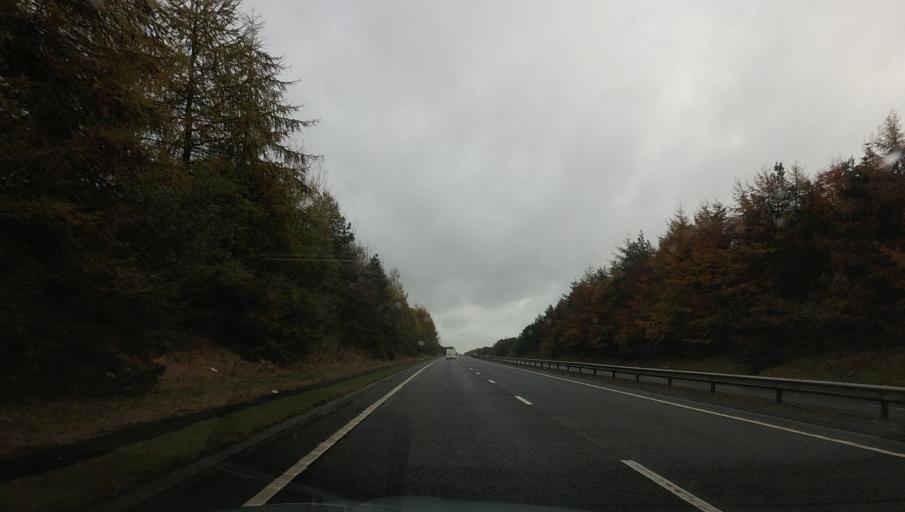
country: GB
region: Scotland
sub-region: Fife
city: Cardenden
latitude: 56.1340
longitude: -3.2357
